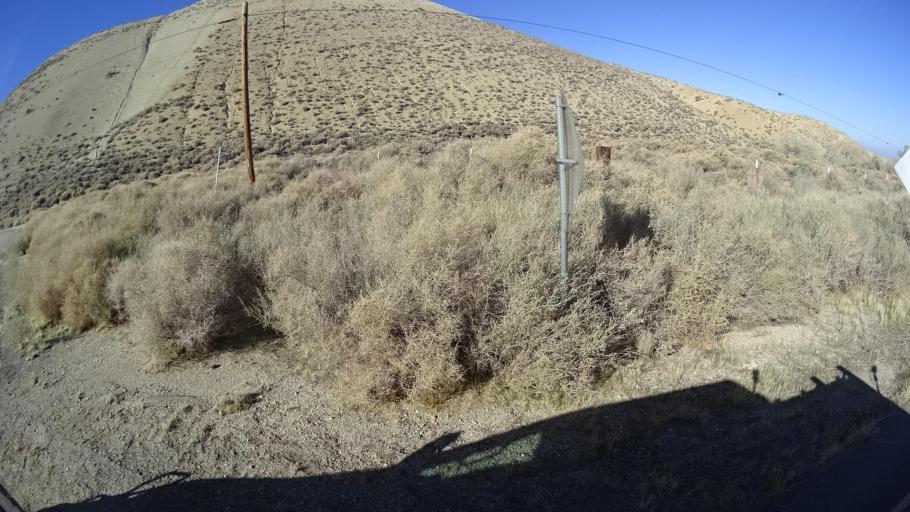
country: US
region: California
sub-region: Kern County
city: Maricopa
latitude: 34.9785
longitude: -119.4038
